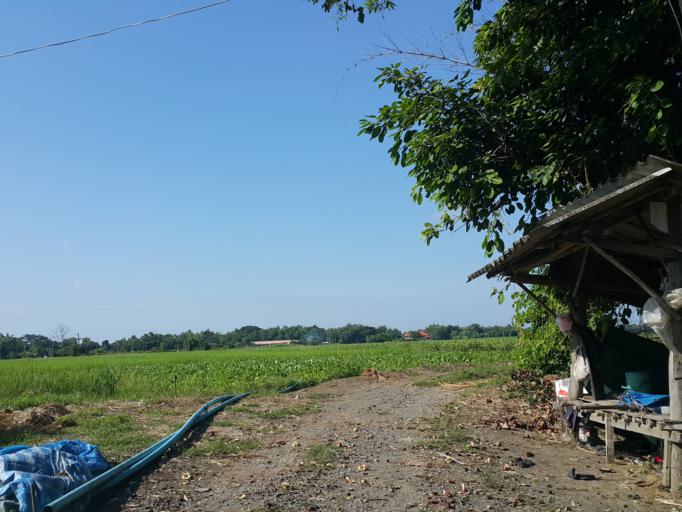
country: TH
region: Chiang Mai
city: San Kamphaeng
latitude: 18.8234
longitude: 99.1605
